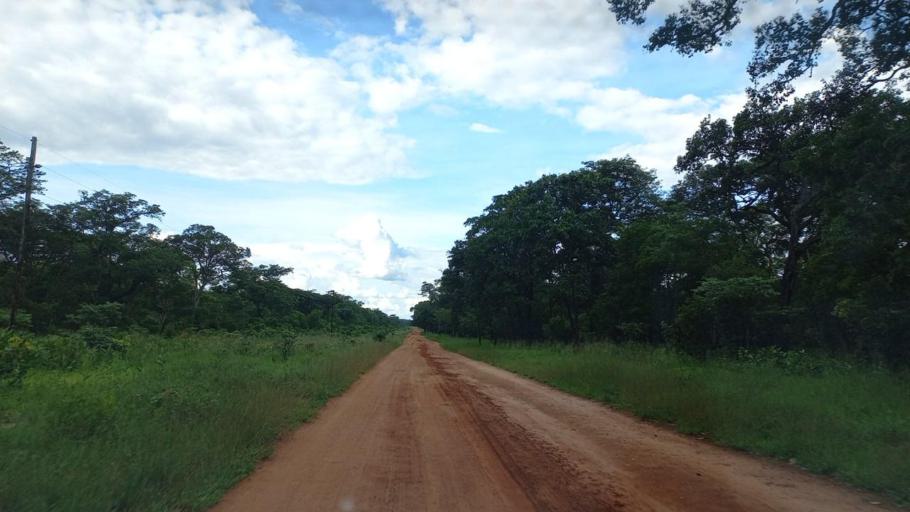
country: ZM
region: North-Western
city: Mwinilunga
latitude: -11.8041
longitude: 24.3695
